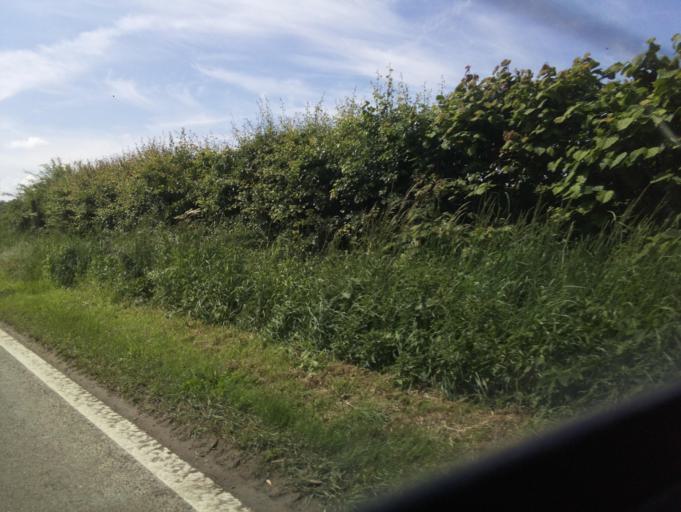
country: GB
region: England
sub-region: North Lincolnshire
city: Manton
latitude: 53.5058
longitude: -0.5826
